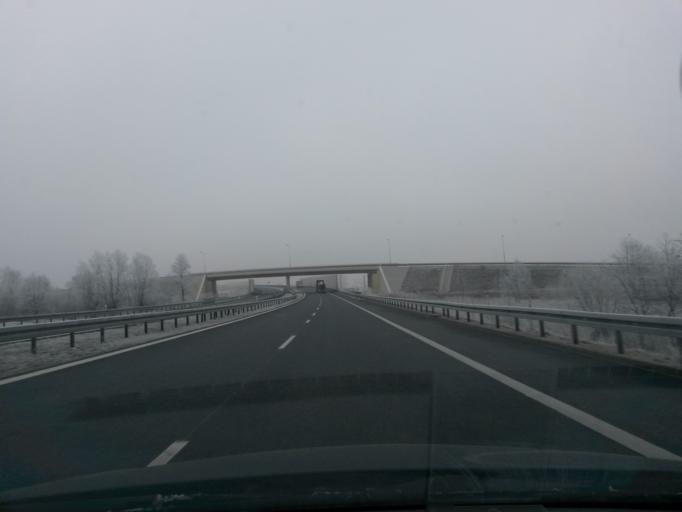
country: PL
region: Greater Poland Voivodeship
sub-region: Powiat gnieznienski
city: Lubowo
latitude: 52.4979
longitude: 17.4570
